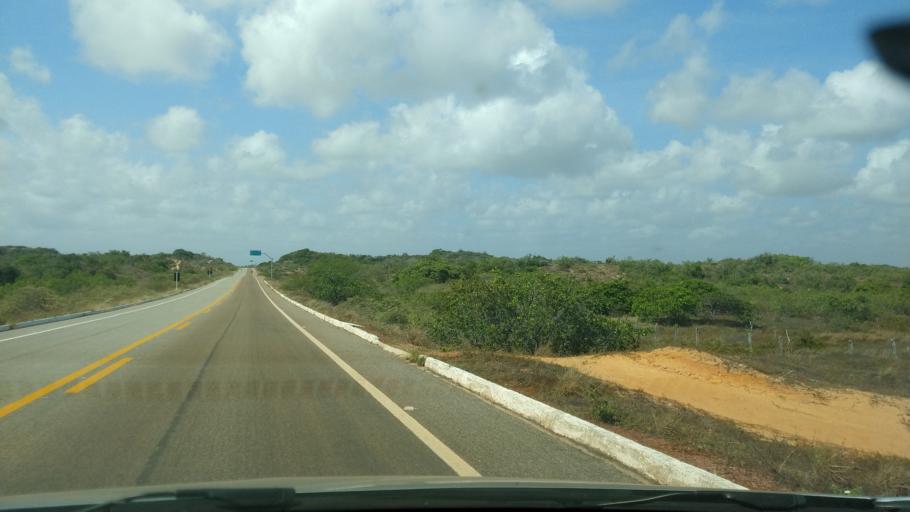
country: BR
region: Rio Grande do Norte
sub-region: Touros
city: Touros
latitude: -5.1641
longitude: -35.5026
